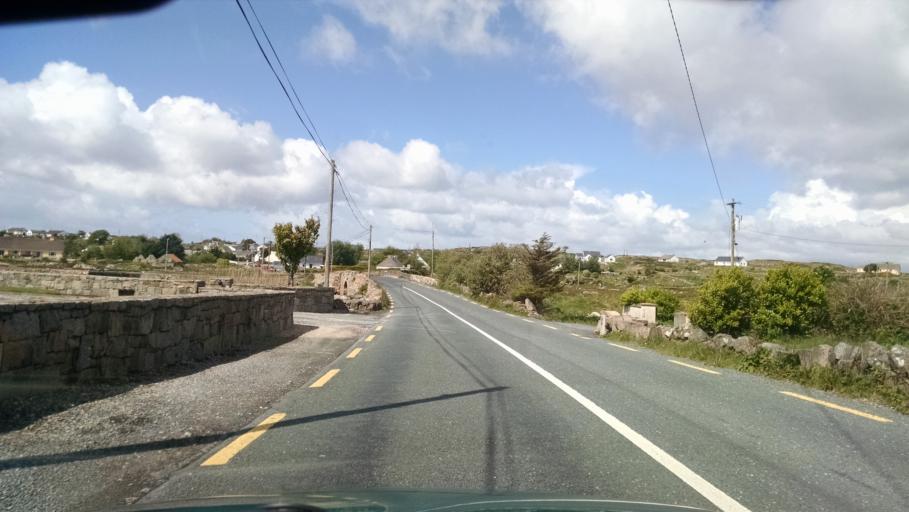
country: IE
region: Connaught
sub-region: County Galway
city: Oughterard
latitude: 53.2893
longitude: -9.5572
